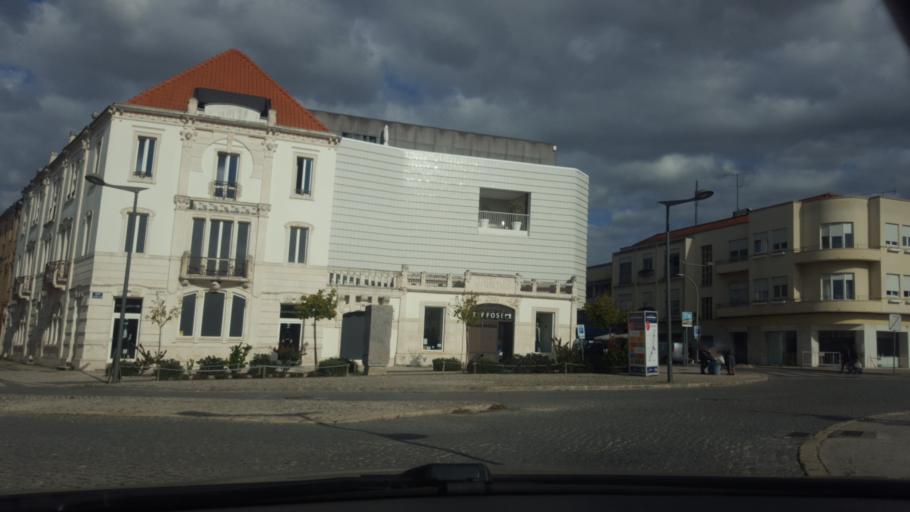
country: PT
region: Leiria
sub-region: Leiria
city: Leiria
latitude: 39.7452
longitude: -8.8062
